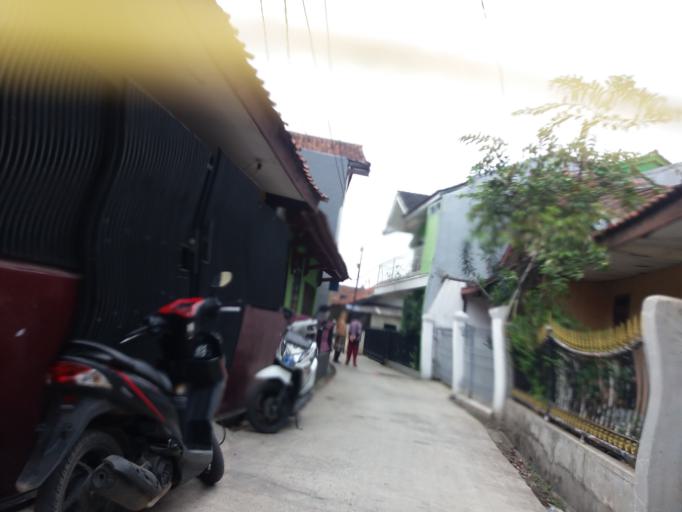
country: ID
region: West Java
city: Bandung
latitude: -6.9213
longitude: 107.6518
